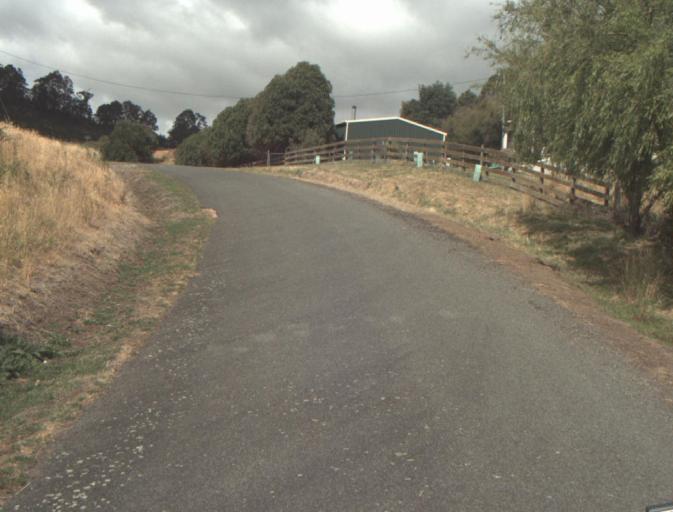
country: AU
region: Tasmania
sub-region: Northern Midlands
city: Evandale
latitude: -41.5142
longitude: 147.4714
